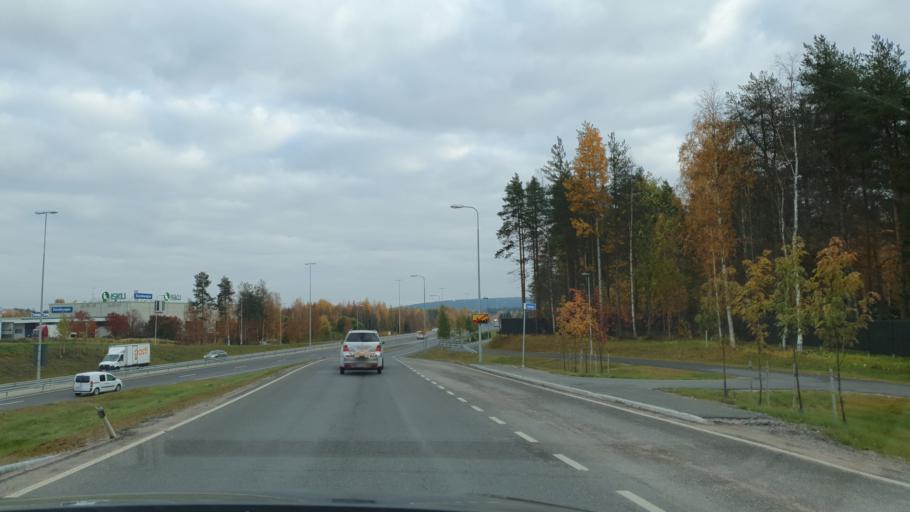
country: FI
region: Lapland
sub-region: Rovaniemi
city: Rovaniemi
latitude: 66.4899
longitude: 25.6935
